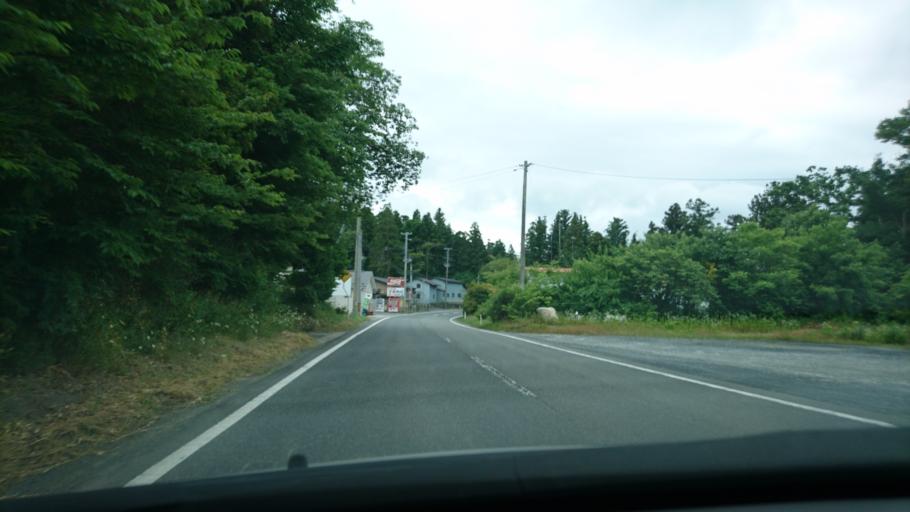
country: JP
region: Iwate
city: Ichinoseki
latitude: 38.7532
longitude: 141.2548
